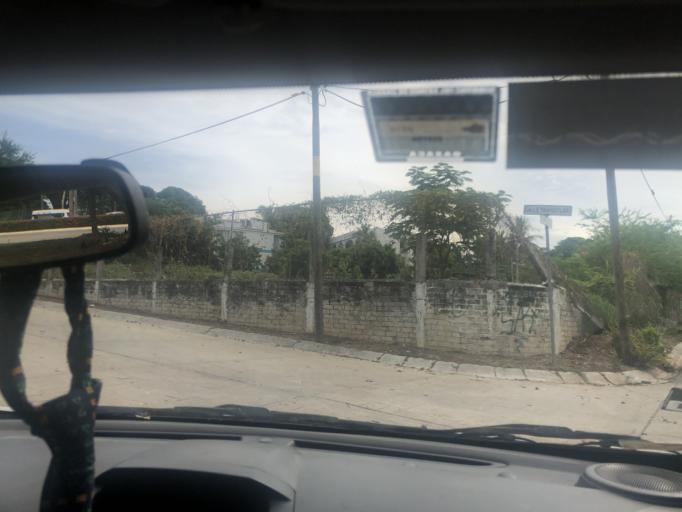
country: MX
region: Oaxaca
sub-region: San Pedro Mixtepec -Dto. 22 -
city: Puerto Escondido
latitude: 15.8647
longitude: -97.0852
